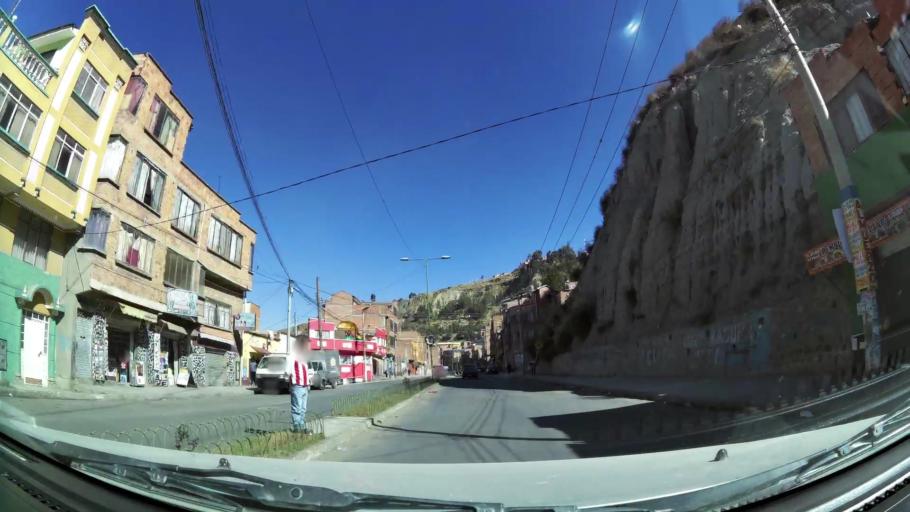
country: BO
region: La Paz
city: La Paz
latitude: -16.5121
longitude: -68.1440
